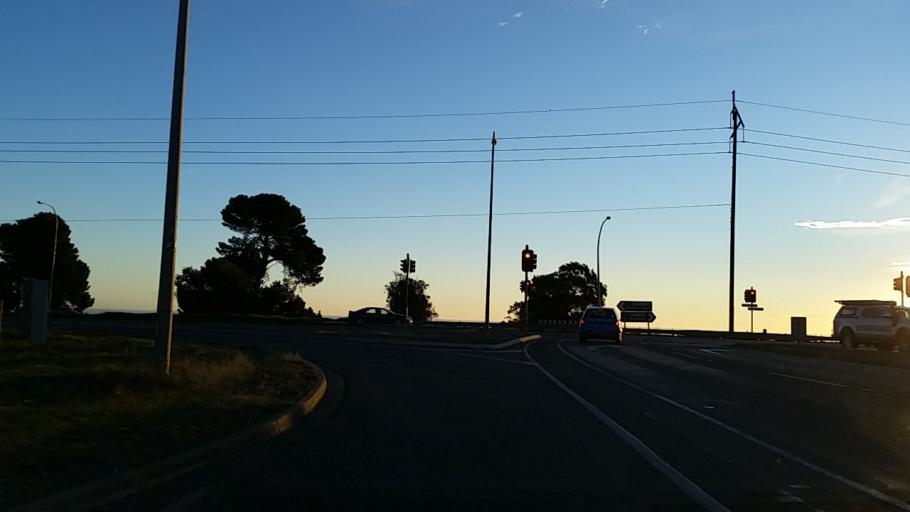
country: AU
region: South Australia
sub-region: Marion
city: Trott Park
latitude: -35.0551
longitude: 138.5357
